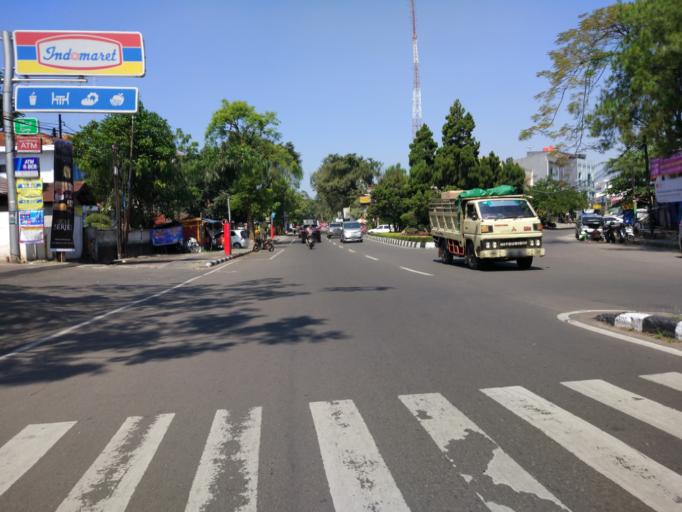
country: ID
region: West Java
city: Bandung
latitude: -6.9241
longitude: 107.6199
